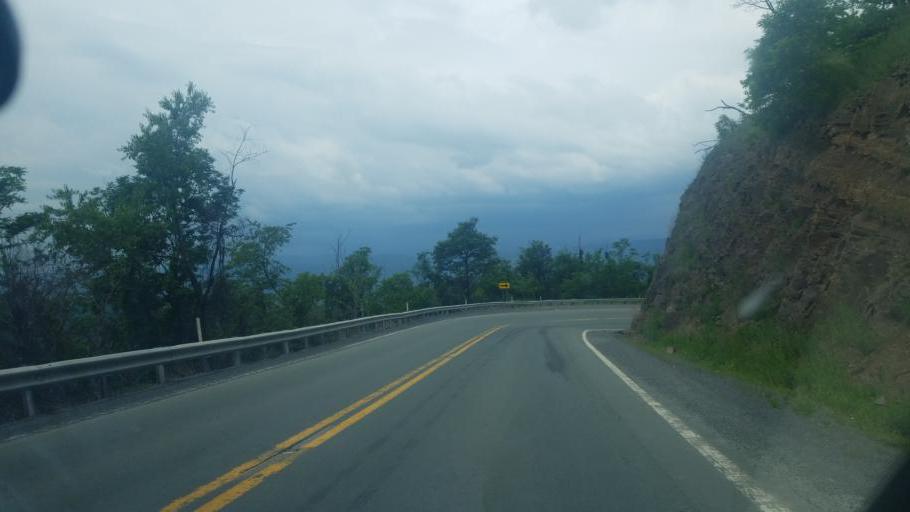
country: US
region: West Virginia
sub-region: Pendleton County
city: Franklin
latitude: 38.5859
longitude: -79.1685
